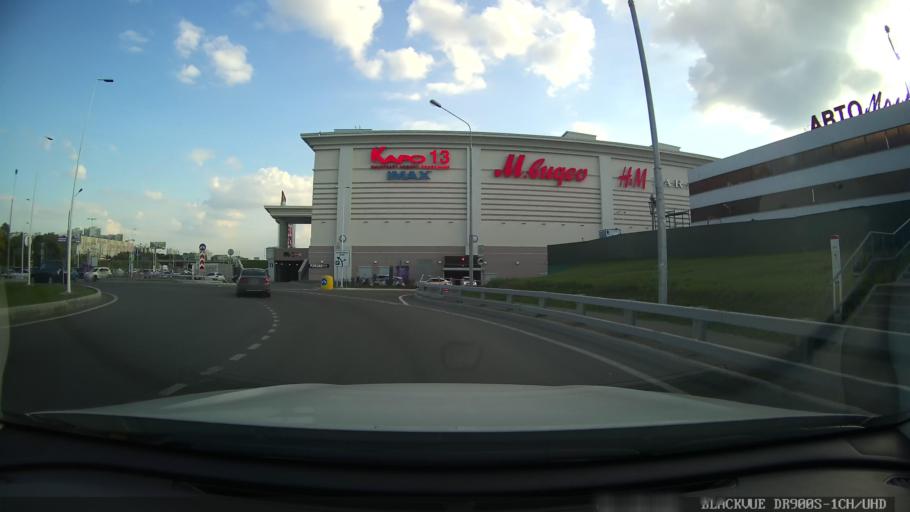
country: RU
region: Moskovskaya
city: Nemchinovka
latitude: 55.7225
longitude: 37.3799
